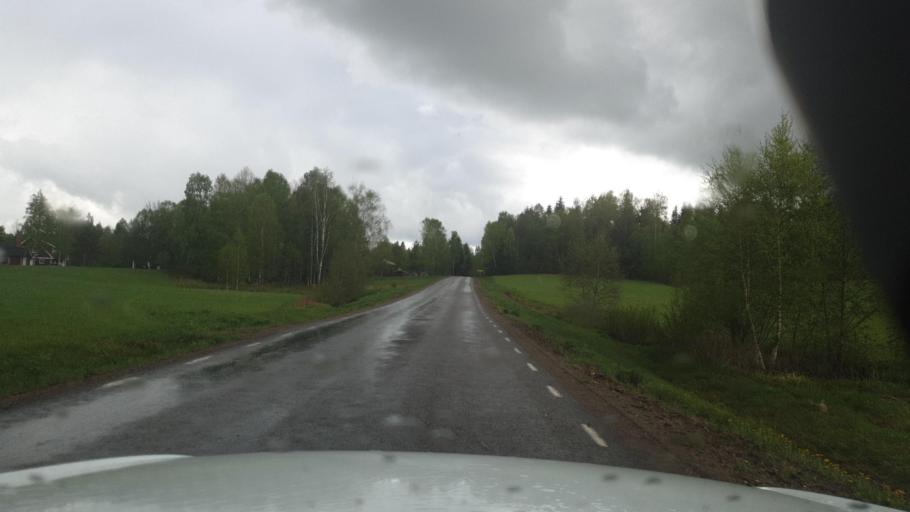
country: SE
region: Vaermland
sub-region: Eda Kommun
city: Charlottenberg
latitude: 59.8041
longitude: 12.1527
